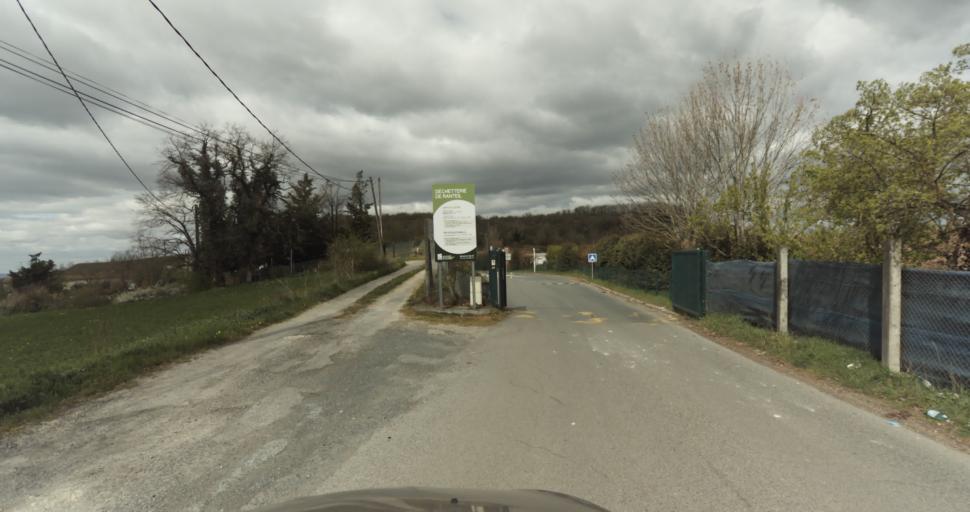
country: FR
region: Midi-Pyrenees
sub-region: Departement du Tarn
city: Puygouzon
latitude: 43.8931
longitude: 2.1428
